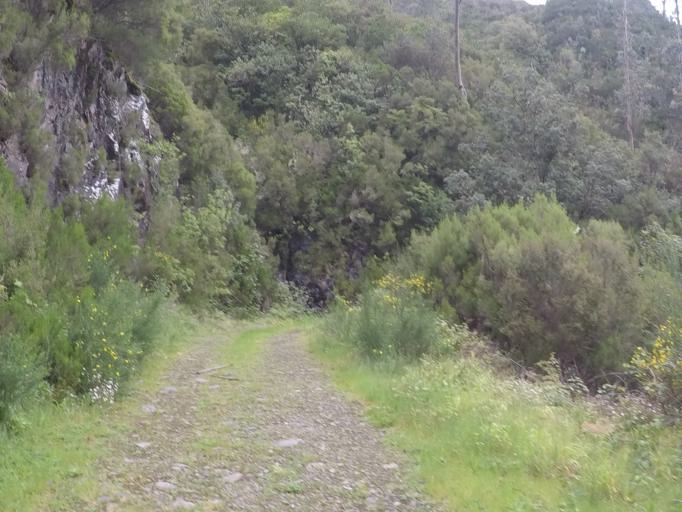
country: PT
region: Madeira
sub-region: Sao Vicente
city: Sao Vicente
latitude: 32.7514
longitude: -17.0178
